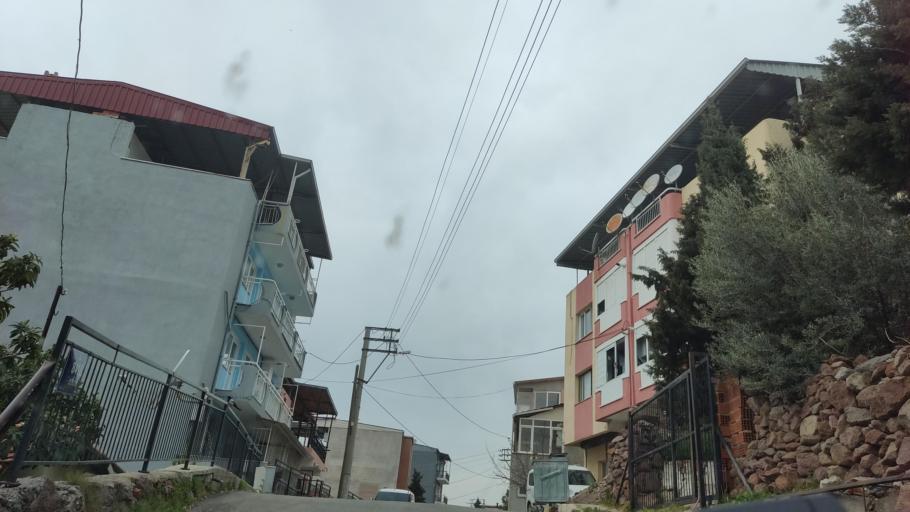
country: TR
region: Izmir
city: Karsiyaka
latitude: 38.4983
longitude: 27.0753
